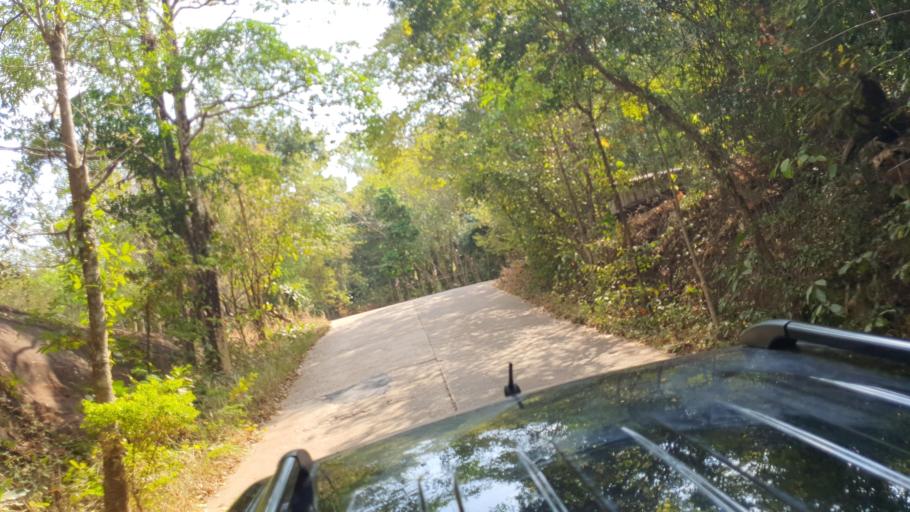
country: TH
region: Changwat Bueng Kan
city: Si Wilai
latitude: 18.2728
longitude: 103.7967
